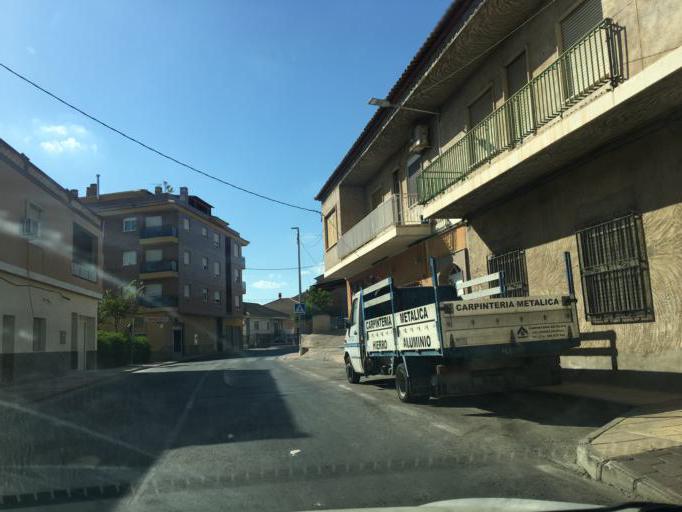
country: ES
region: Murcia
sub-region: Murcia
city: Murcia
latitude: 38.0228
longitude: -1.0885
